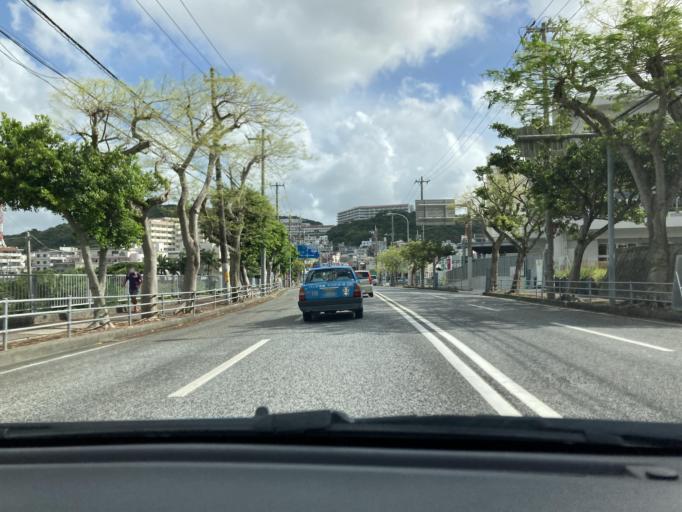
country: JP
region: Okinawa
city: Tomigusuku
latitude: 26.1783
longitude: 127.6814
